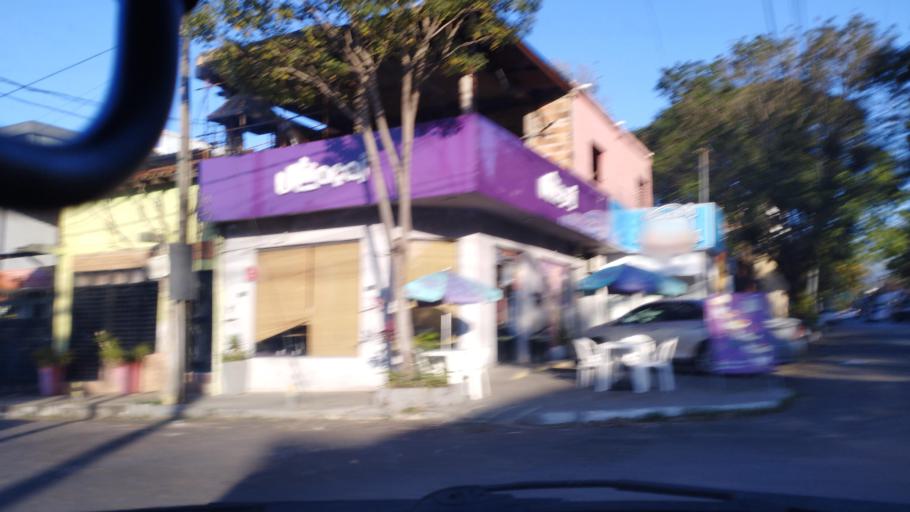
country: PY
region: Central
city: Lambare
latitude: -25.3028
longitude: -57.5853
